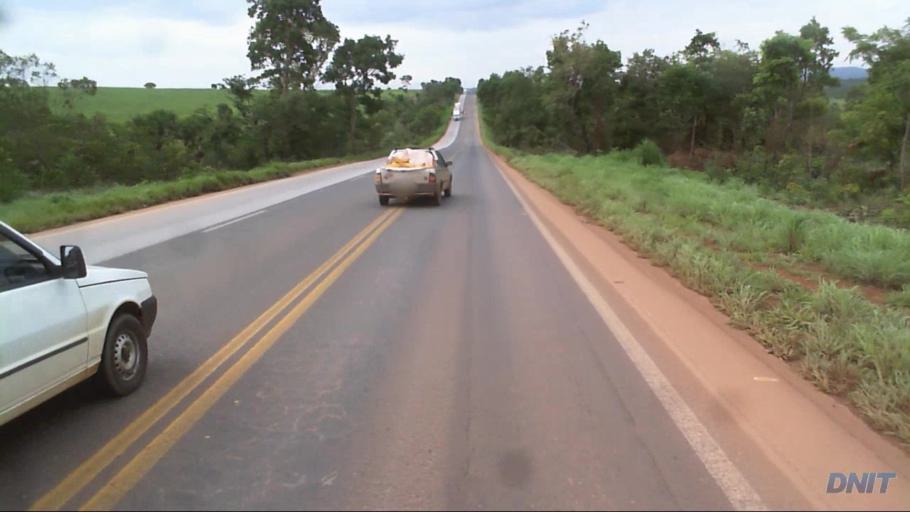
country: BR
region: Goias
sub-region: Uruacu
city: Uruacu
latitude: -14.5786
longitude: -49.1590
